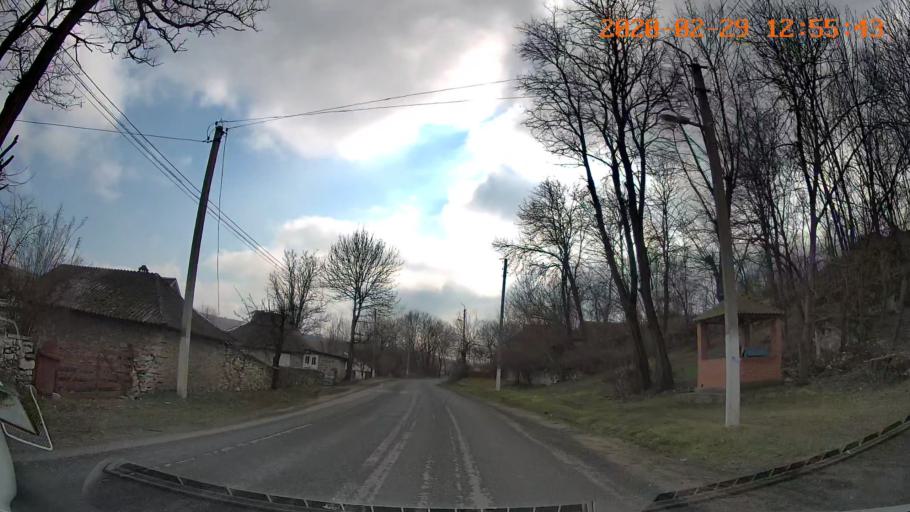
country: MD
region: Telenesti
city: Camenca
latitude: 48.0924
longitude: 28.7242
